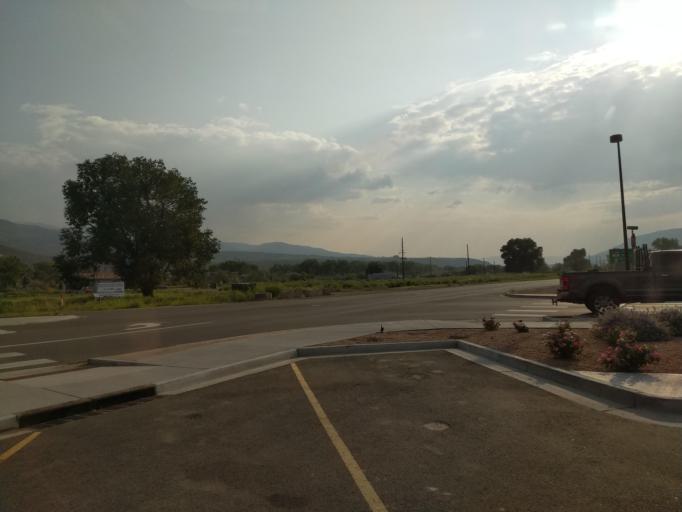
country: US
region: Colorado
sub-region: Garfield County
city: Rifle
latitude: 39.5298
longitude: -107.7842
